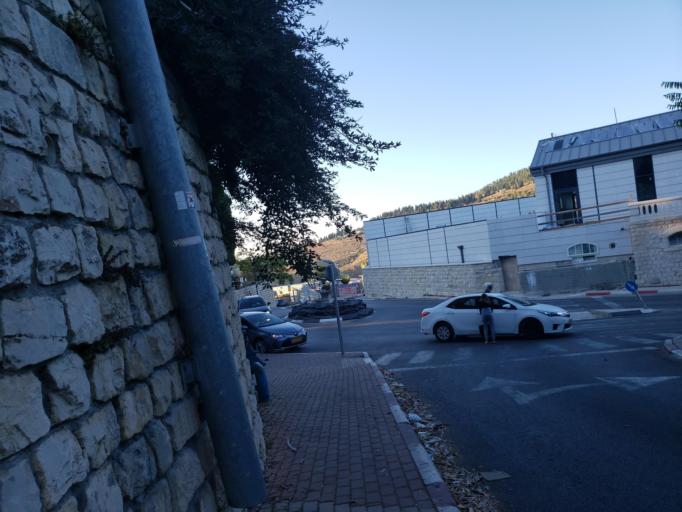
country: IL
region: Northern District
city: Safed
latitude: 32.9711
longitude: 35.4953
